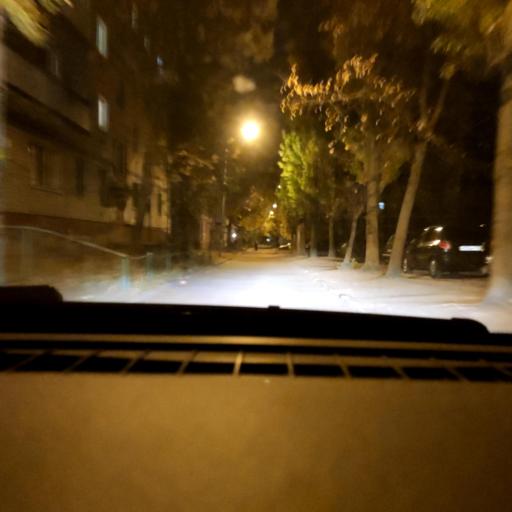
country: RU
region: Voronezj
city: Maslovka
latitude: 51.6347
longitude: 39.2709
